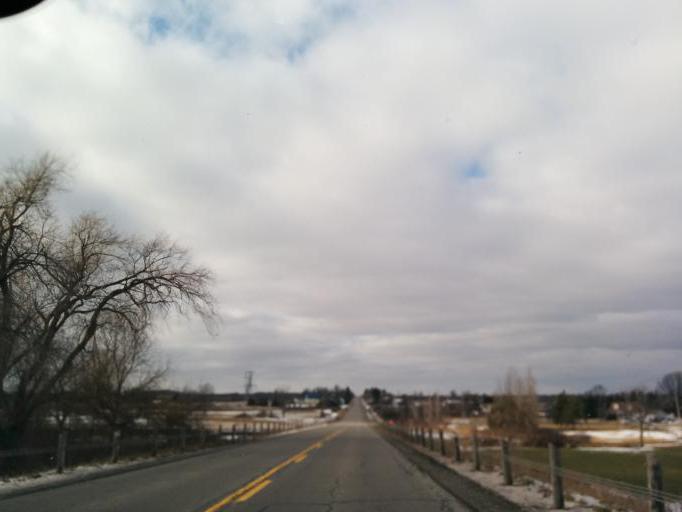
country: CA
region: Ontario
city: Brantford
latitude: 42.9747
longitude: -80.0862
